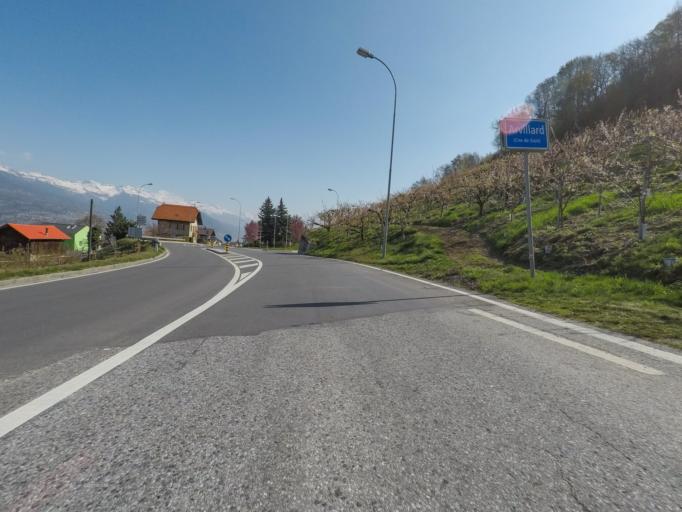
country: CH
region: Valais
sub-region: Sion District
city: Sitten
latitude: 46.2091
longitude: 7.3423
